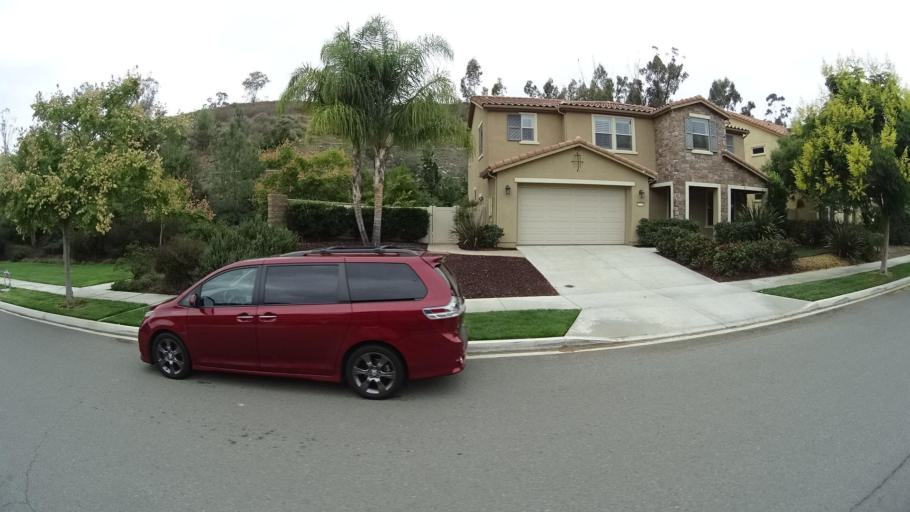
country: US
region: California
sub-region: San Diego County
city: Fairbanks Ranch
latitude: 33.0332
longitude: -117.1131
